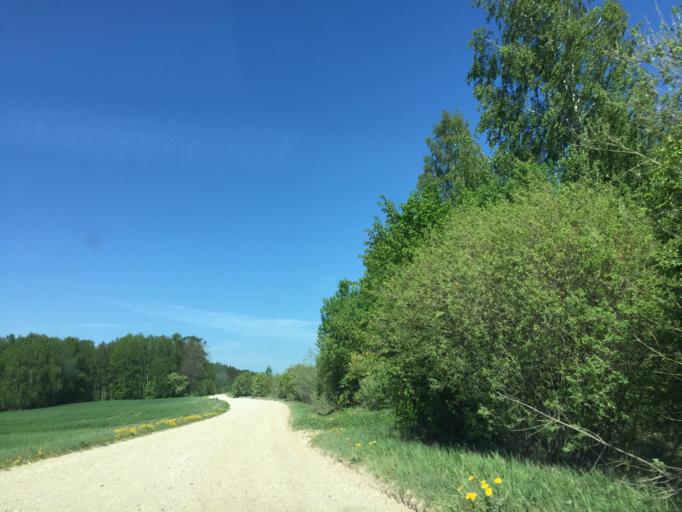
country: LV
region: Ikskile
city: Ikskile
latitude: 56.8744
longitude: 24.4984
